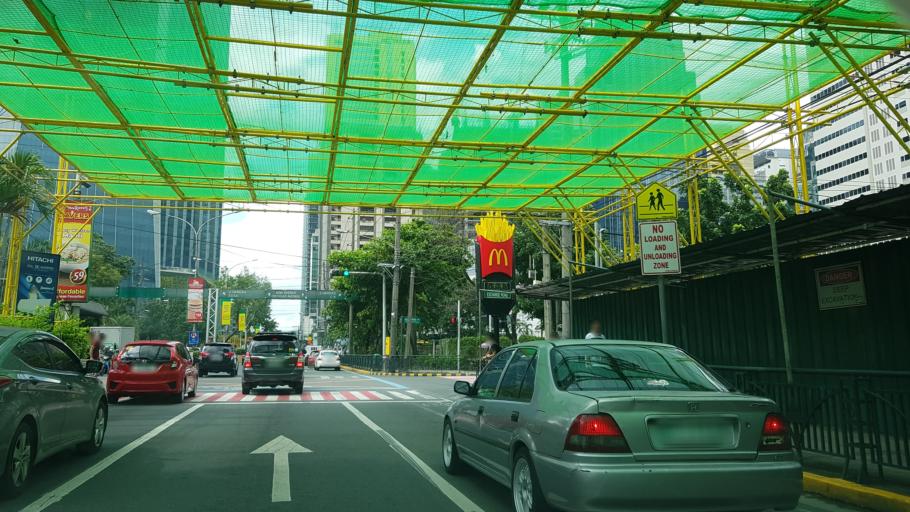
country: PH
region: Metro Manila
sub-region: Pasig
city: Pasig City
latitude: 14.5827
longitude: 121.0601
